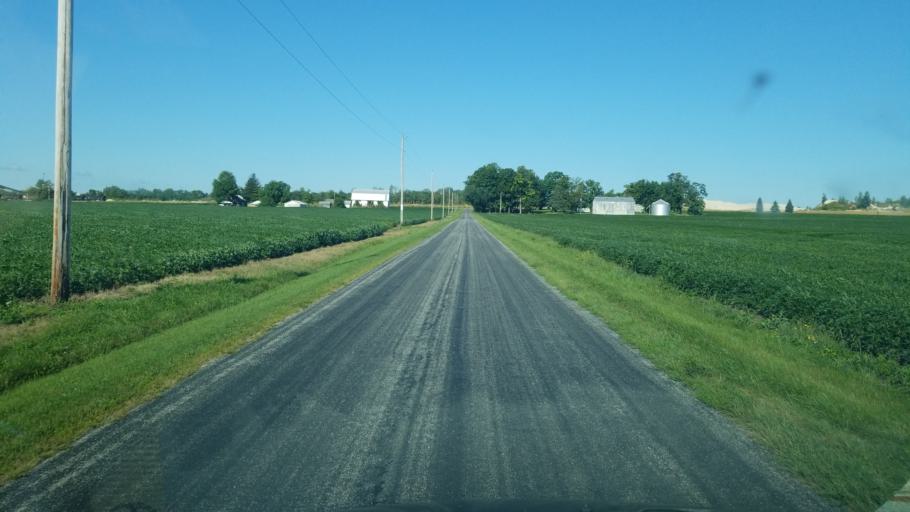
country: US
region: Ohio
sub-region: Wyandot County
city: Carey
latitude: 40.9719
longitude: -83.3613
